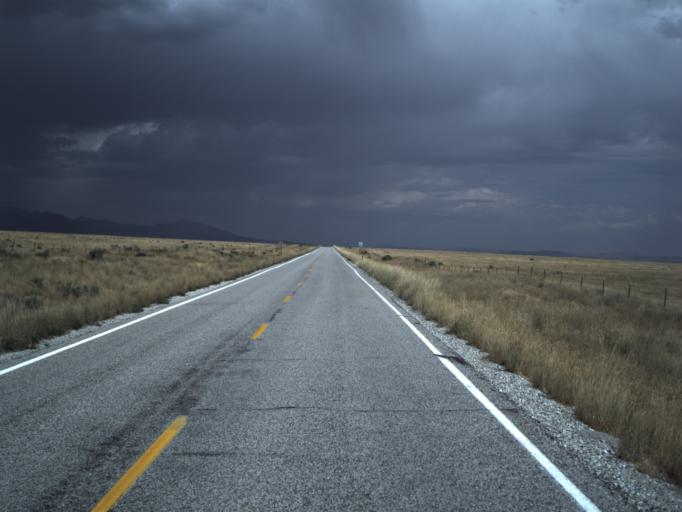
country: US
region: Idaho
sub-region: Minidoka County
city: Rupert
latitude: 41.8497
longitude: -113.1348
